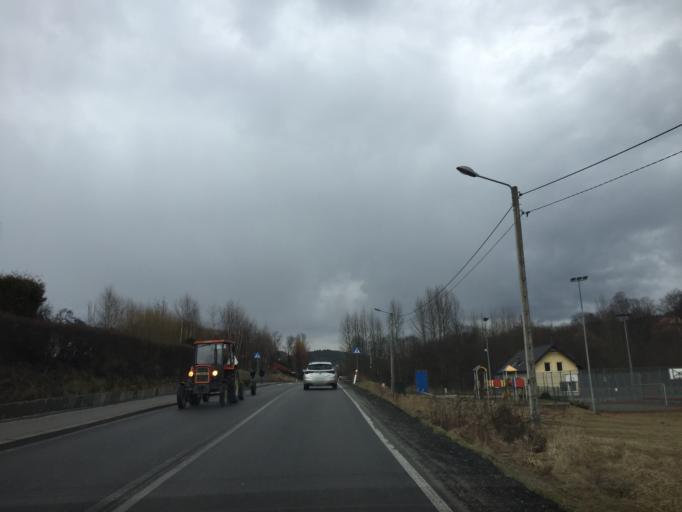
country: PL
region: Lesser Poland Voivodeship
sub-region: Powiat suski
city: Palcza
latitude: 49.8002
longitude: 19.7343
